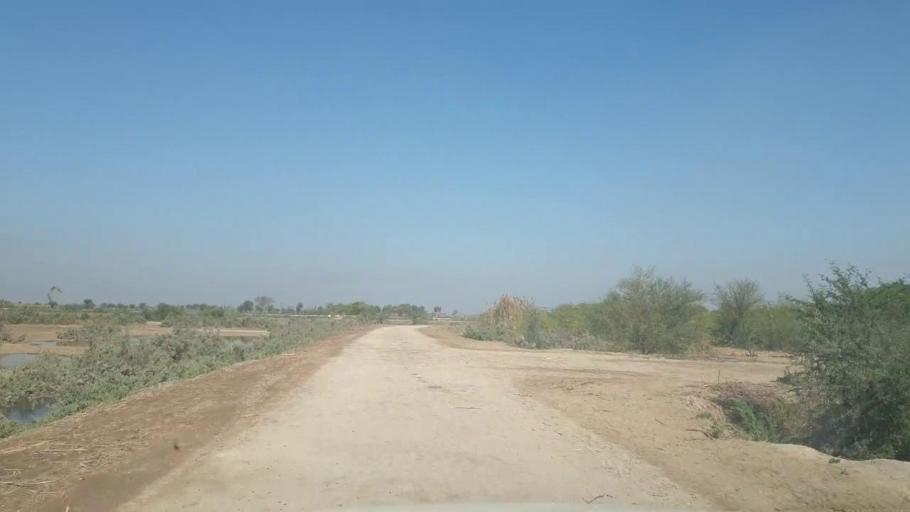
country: PK
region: Sindh
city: Mirpur Khas
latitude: 25.5188
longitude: 69.1615
